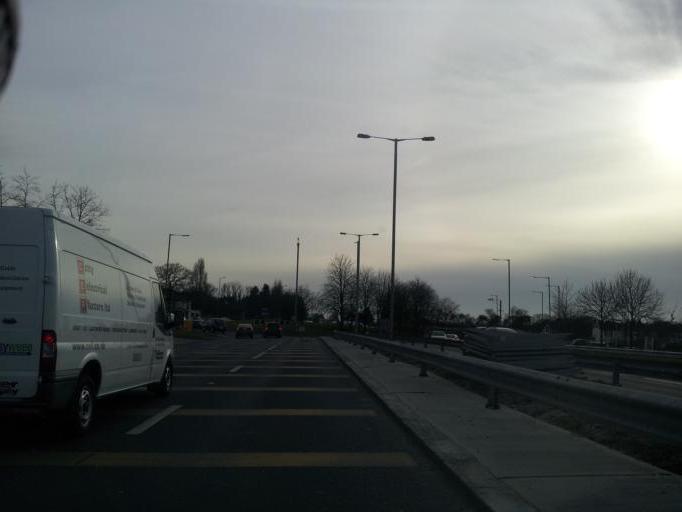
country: GB
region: England
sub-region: Hertfordshire
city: Borehamwood
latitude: 51.6441
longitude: -0.2539
